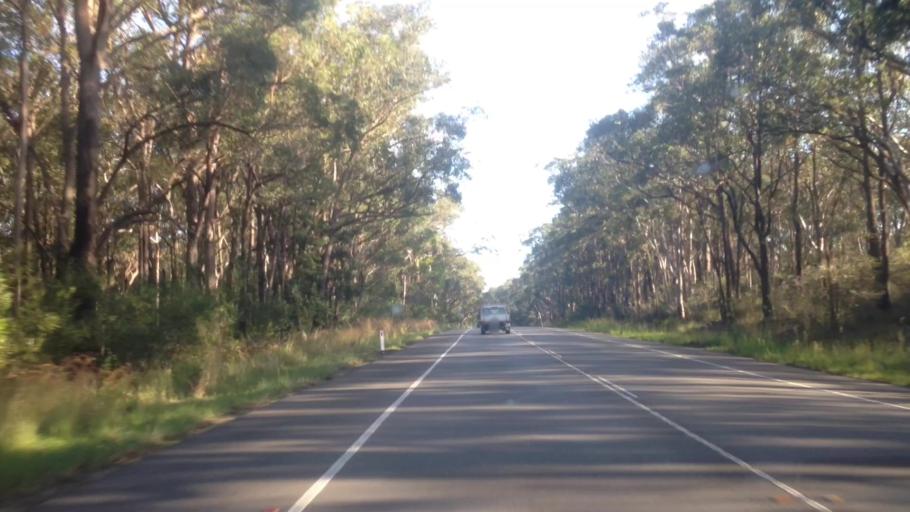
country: AU
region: New South Wales
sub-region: Lake Macquarie Shire
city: Dora Creek
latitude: -33.1367
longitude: 151.4773
